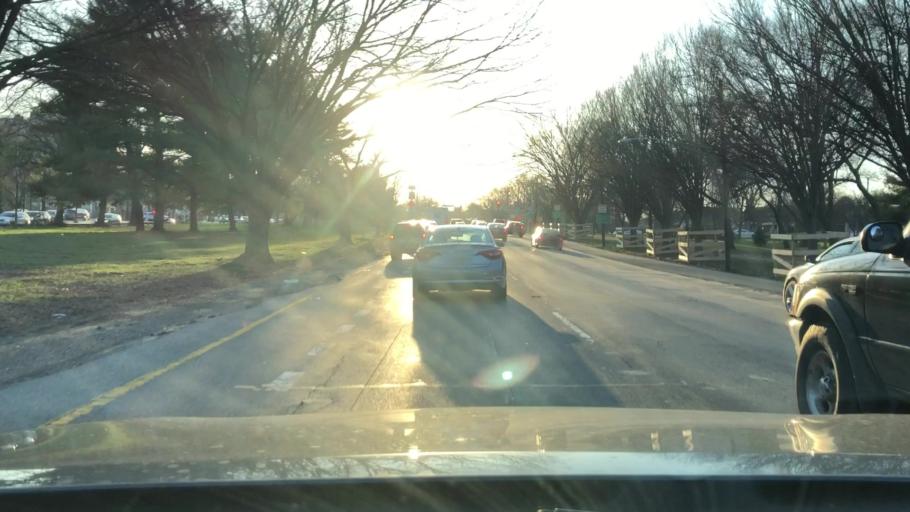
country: US
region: New York
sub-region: Bronx
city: The Bronx
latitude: 40.8574
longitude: -73.8418
